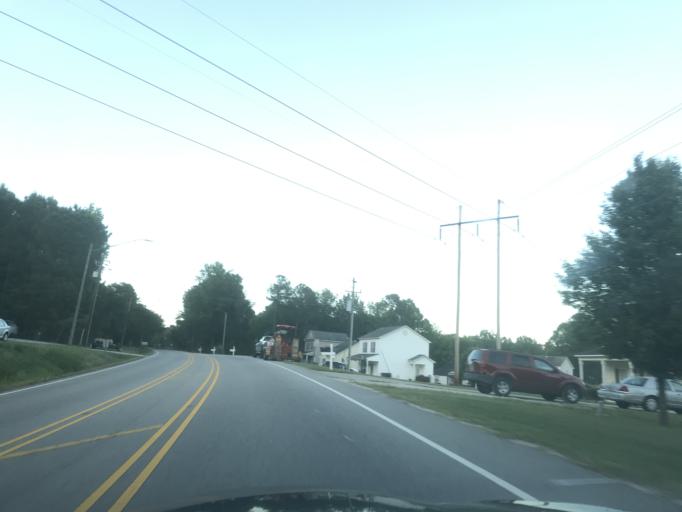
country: US
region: North Carolina
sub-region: Wake County
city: Wendell
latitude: 35.7768
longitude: -78.3783
